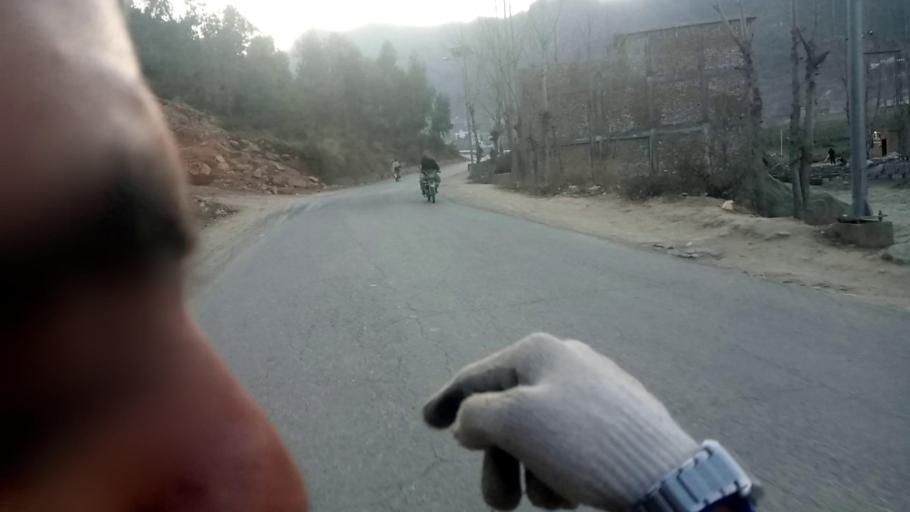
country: PK
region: Khyber Pakhtunkhwa
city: Saidu Sharif
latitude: 34.7365
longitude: 72.3372
